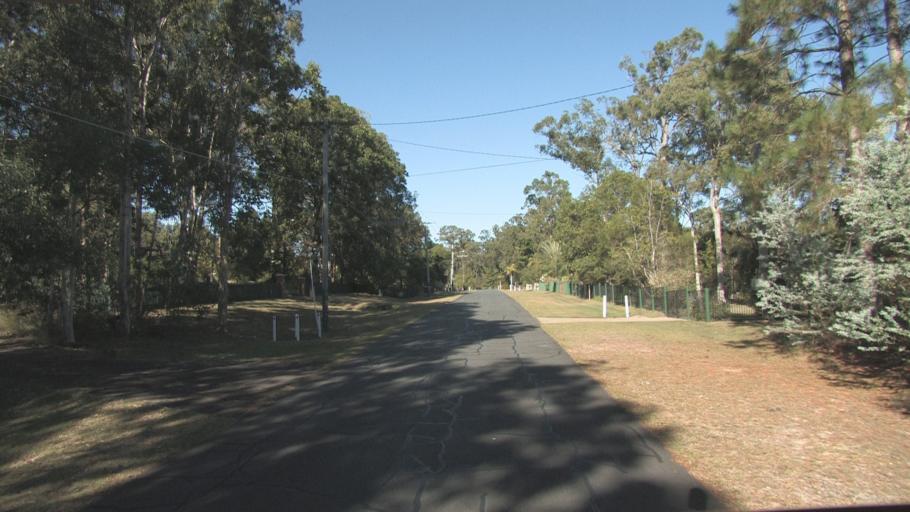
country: AU
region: Queensland
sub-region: Brisbane
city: Forest Lake
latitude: -27.6636
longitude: 153.0113
